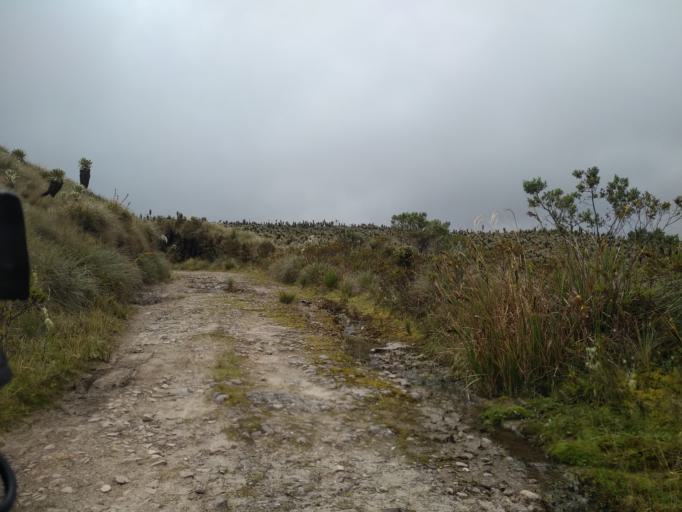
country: EC
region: Carchi
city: San Gabriel
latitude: 0.6856
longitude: -77.8530
